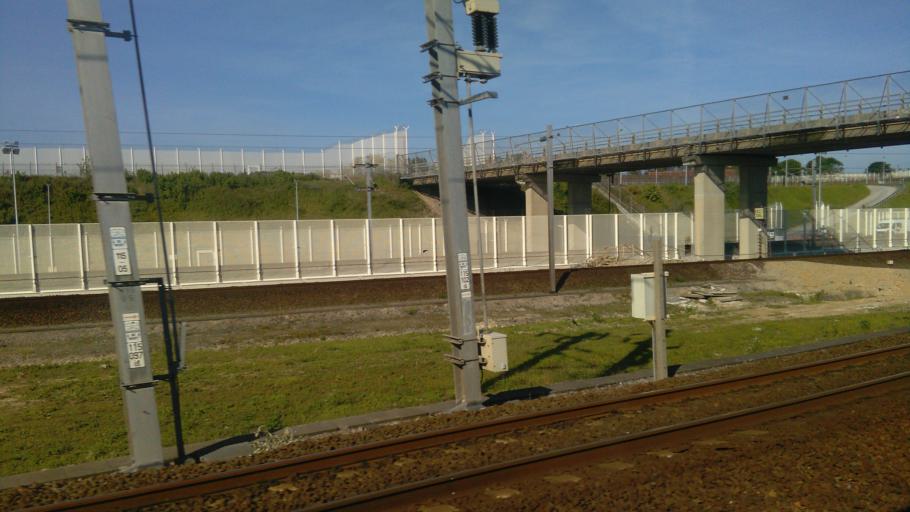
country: FR
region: Nord-Pas-de-Calais
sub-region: Departement du Pas-de-Calais
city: Coquelles
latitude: 50.9189
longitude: 1.7911
